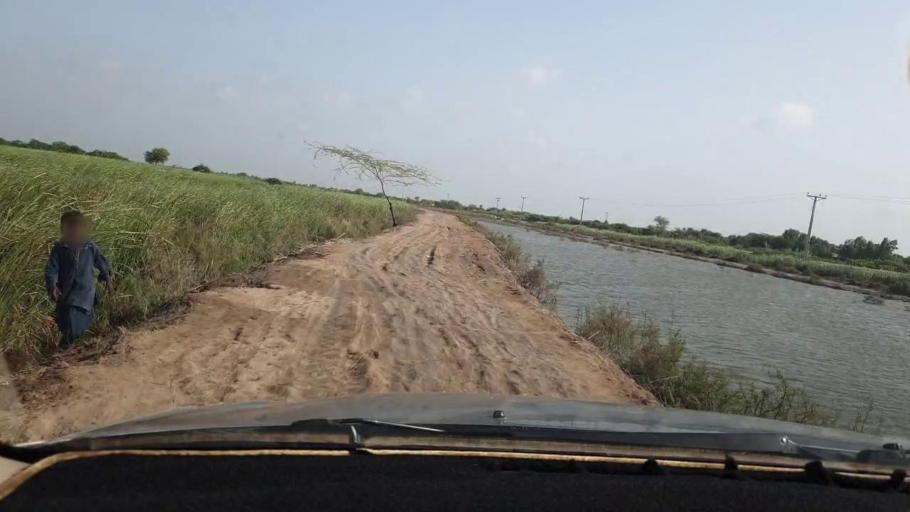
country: PK
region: Sindh
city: Tando Bago
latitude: 24.8141
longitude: 68.9359
